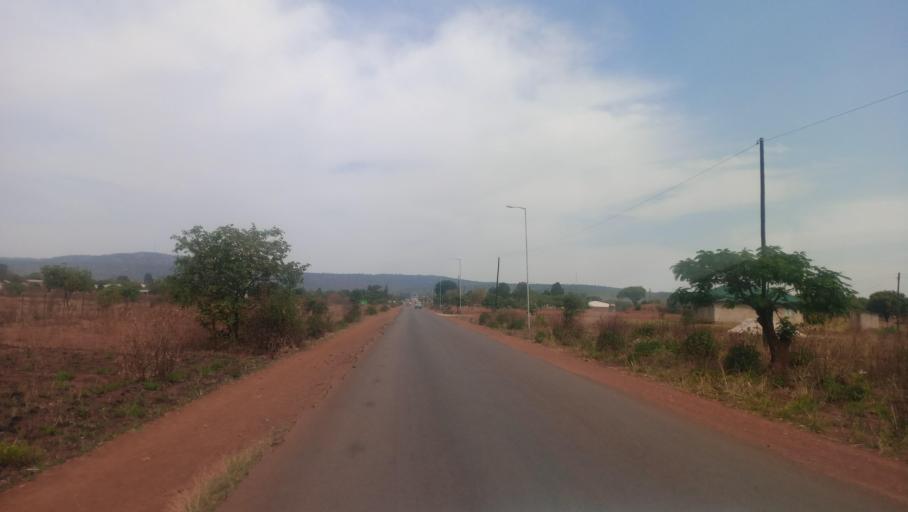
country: ZM
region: Northern
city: Mpika
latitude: -11.8381
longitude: 31.4327
